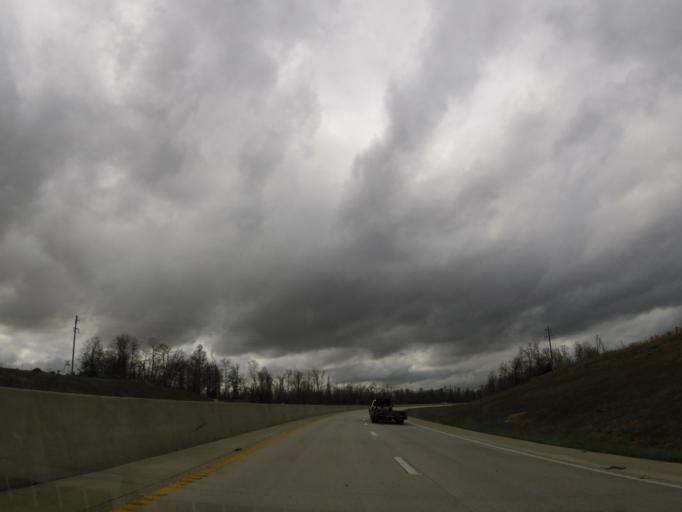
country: US
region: Missouri
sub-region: Butler County
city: Poplar Bluff
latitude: 36.6756
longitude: -90.4887
